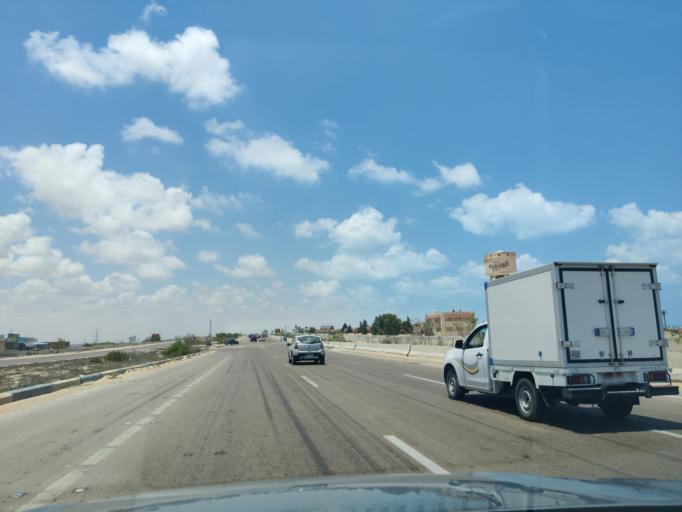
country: EG
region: Muhafazat Matruh
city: Al `Alamayn
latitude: 30.8315
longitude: 29.2201
